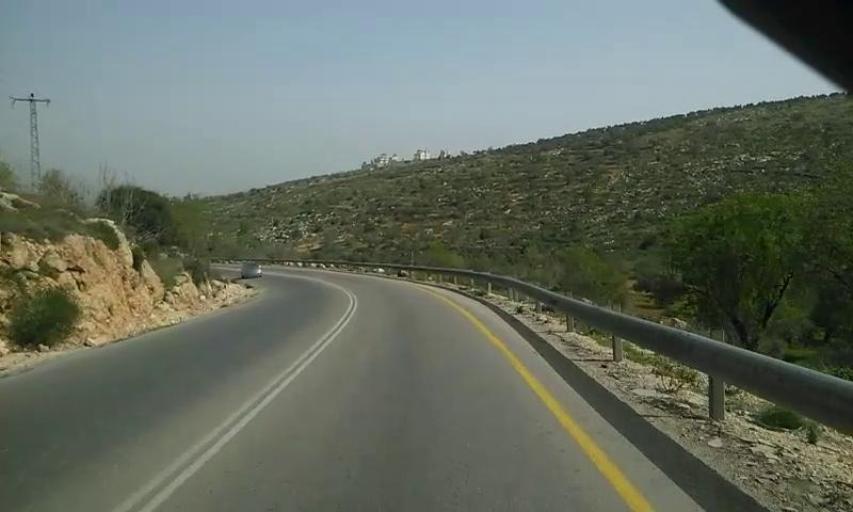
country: PS
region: West Bank
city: Yatma
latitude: 32.1256
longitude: 35.2565
